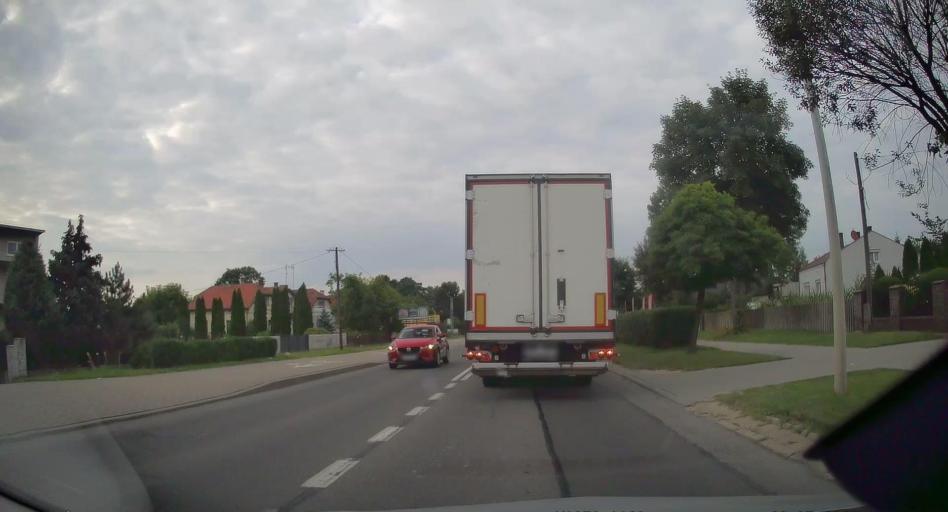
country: PL
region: Lodz Voivodeship
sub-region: Powiat radomszczanski
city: Radomsko
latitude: 51.0575
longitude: 19.4410
